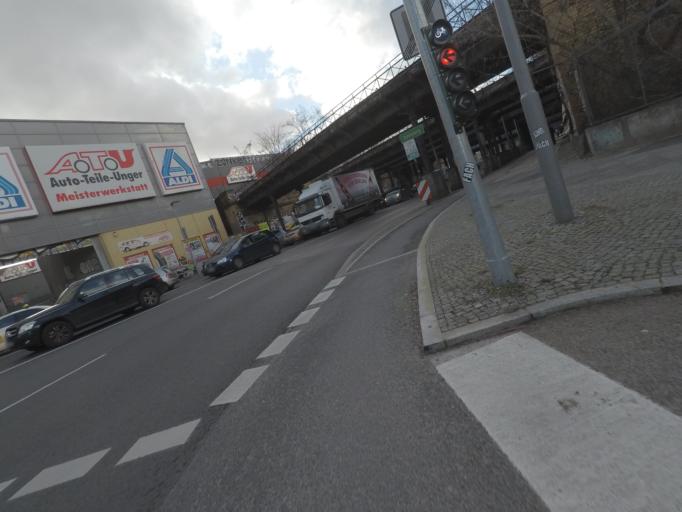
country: DE
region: Berlin
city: Tiergarten Bezirk
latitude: 52.4916
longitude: 13.3765
